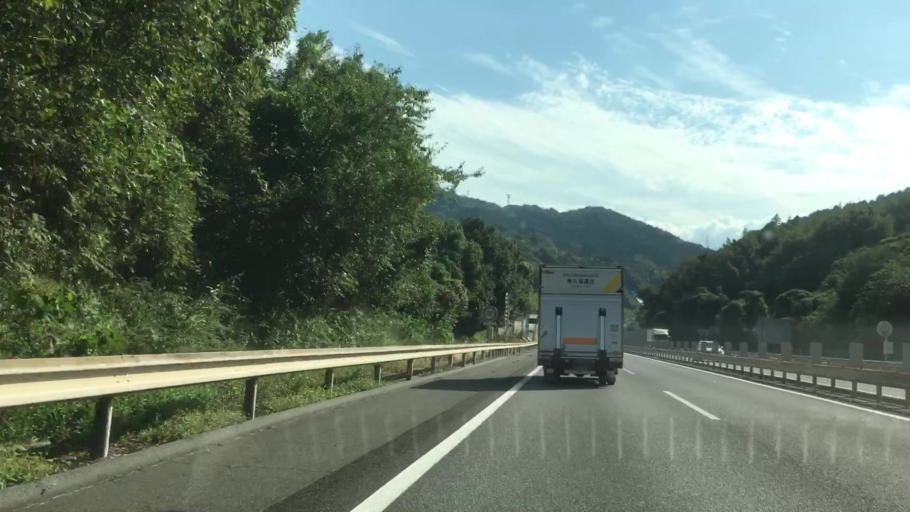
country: JP
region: Yamaguchi
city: Otake
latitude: 34.2387
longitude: 132.2146
